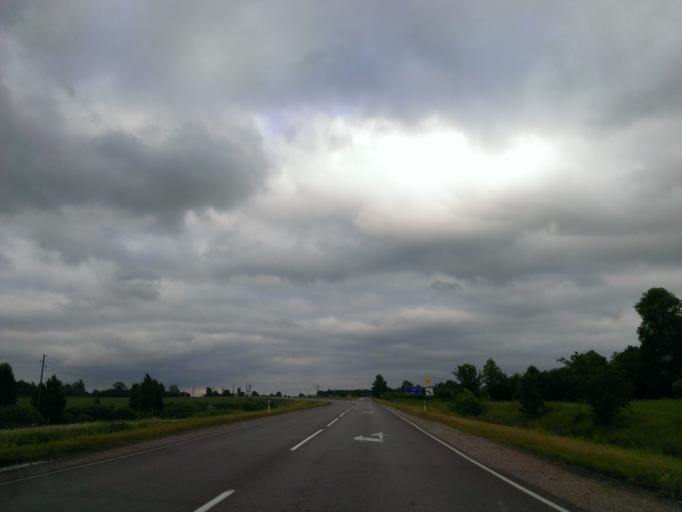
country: LV
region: Saldus Rajons
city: Saldus
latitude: 56.6690
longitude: 22.4109
